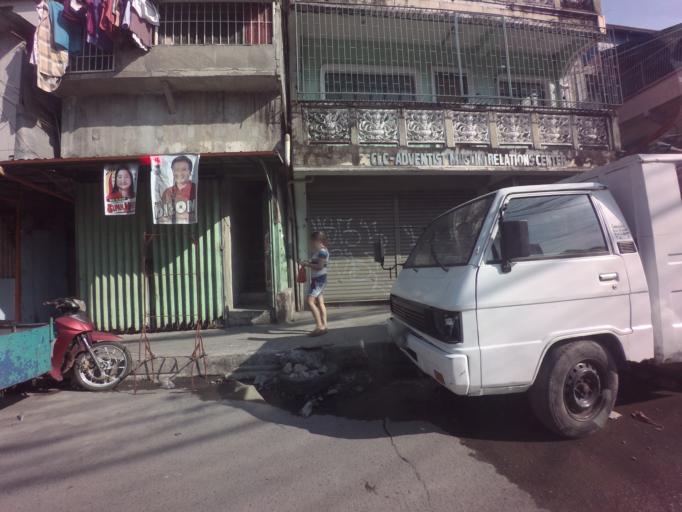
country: PH
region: Calabarzon
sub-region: Province of Rizal
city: Taguig
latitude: 14.4960
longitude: 121.0536
